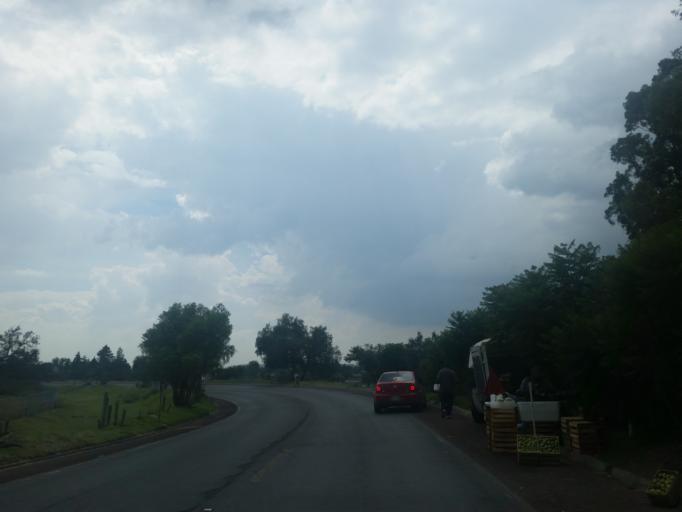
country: MX
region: Mexico
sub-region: Teotihuacan
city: Teotihuacan de Arista
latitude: 19.6842
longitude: -98.8541
